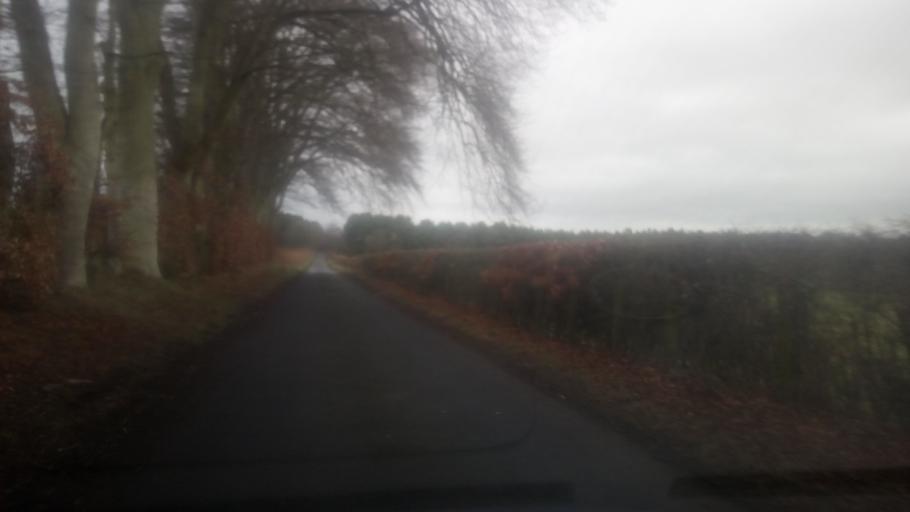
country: GB
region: Scotland
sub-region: The Scottish Borders
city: Jedburgh
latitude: 55.5404
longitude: -2.4947
